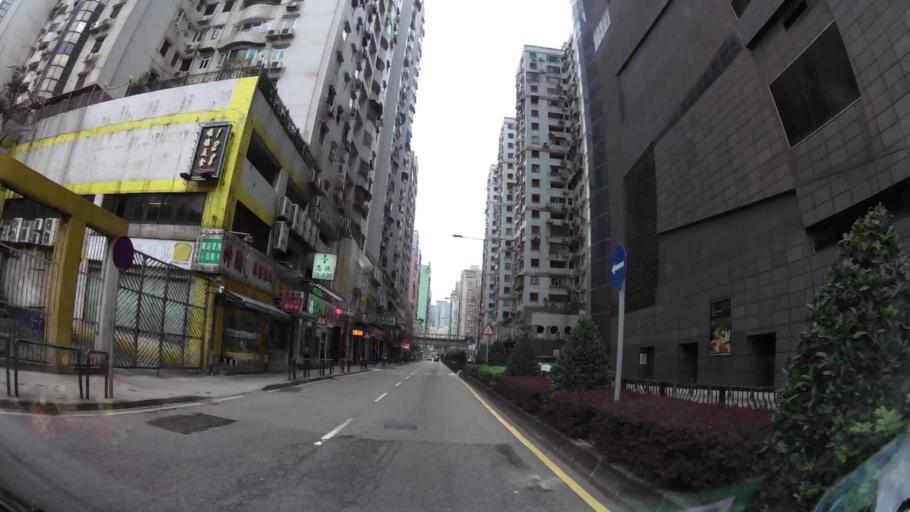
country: MO
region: Macau
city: Macau
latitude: 22.1621
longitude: 113.5553
